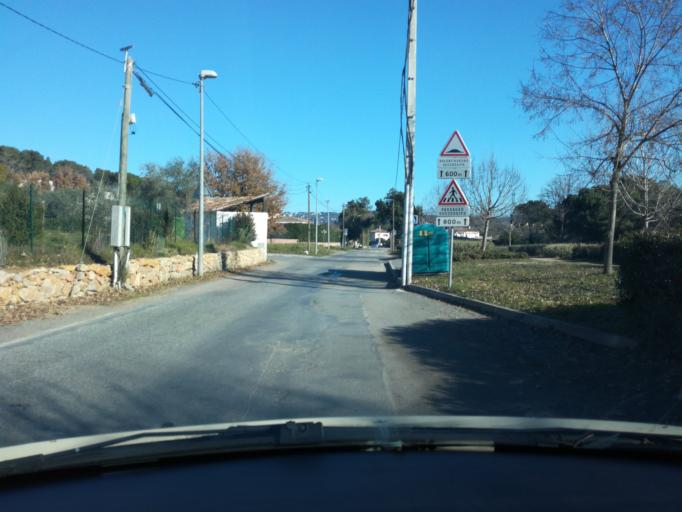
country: FR
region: Provence-Alpes-Cote d'Azur
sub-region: Departement des Alpes-Maritimes
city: La Roquette-sur-Siagne
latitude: 43.6016
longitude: 6.9508
